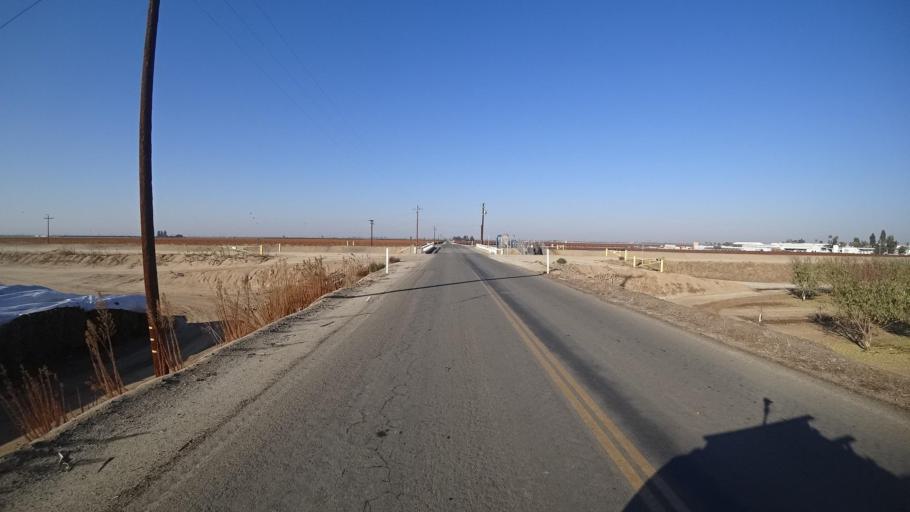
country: US
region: California
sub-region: Kern County
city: Delano
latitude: 35.7687
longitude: -119.1763
